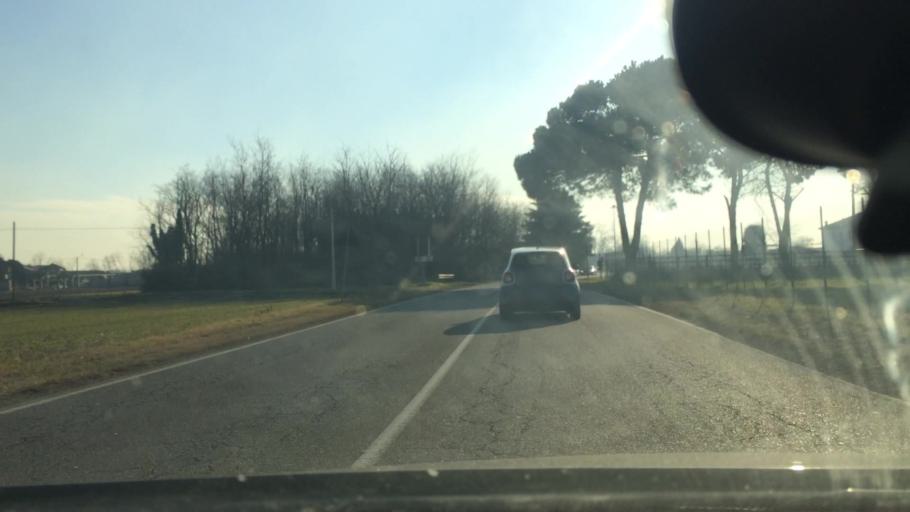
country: IT
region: Lombardy
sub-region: Citta metropolitana di Milano
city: Arluno
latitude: 45.5076
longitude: 8.9302
